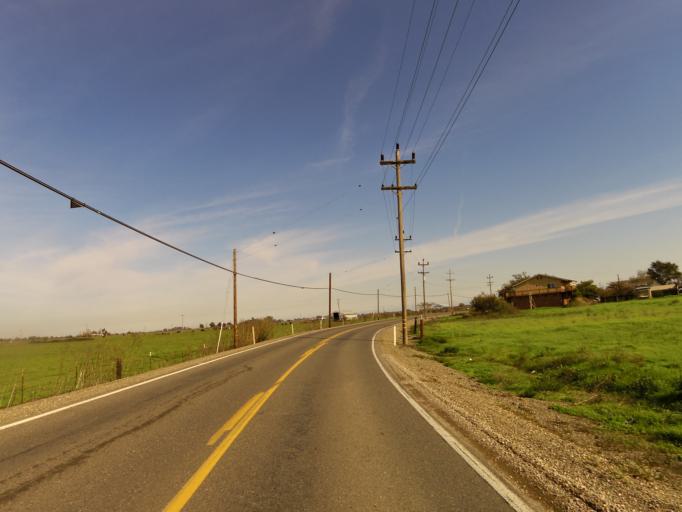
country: US
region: California
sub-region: San Joaquin County
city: Thornton
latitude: 38.2896
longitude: -121.4497
